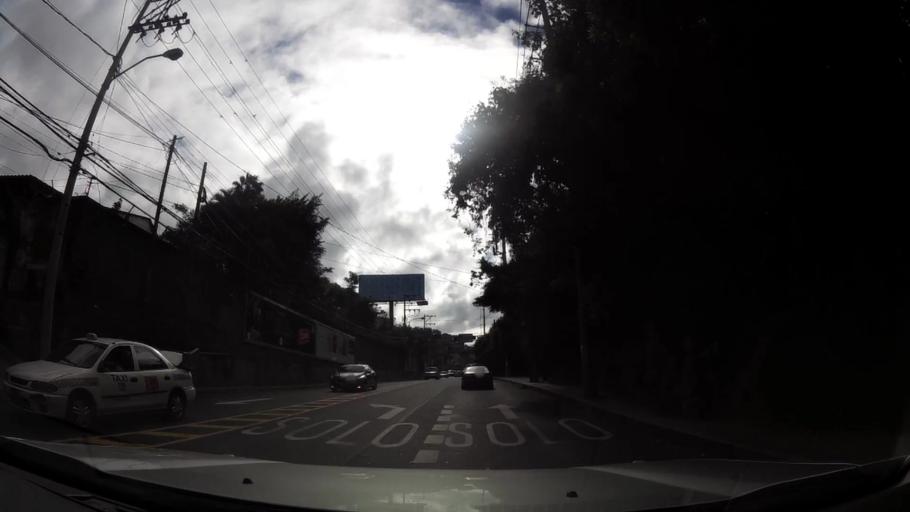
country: GT
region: Guatemala
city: Santa Catarina Pinula
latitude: 14.5772
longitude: -90.4922
